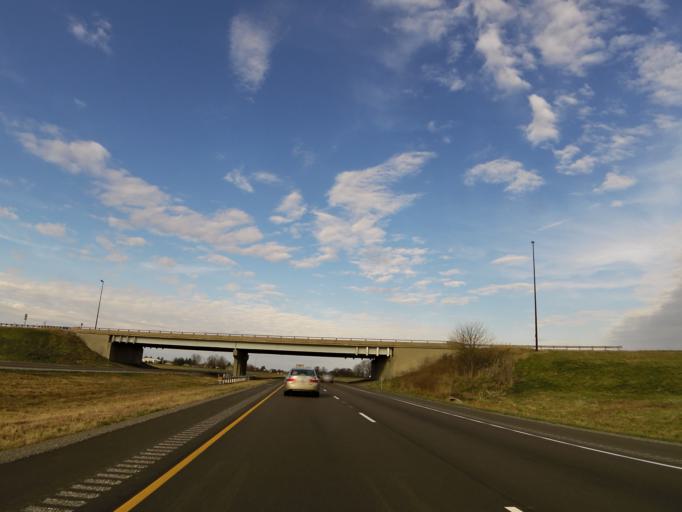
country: US
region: Illinois
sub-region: Washington County
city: Okawville
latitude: 38.4393
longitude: -89.5291
